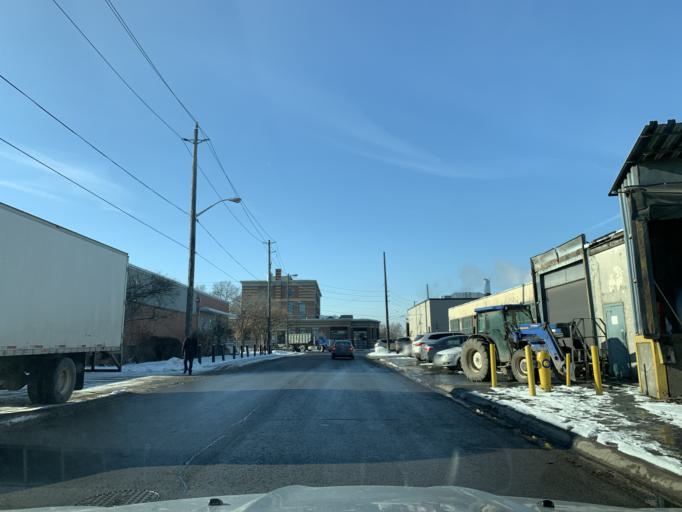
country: CA
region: Ontario
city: Toronto
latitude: 43.6740
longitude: -79.4764
